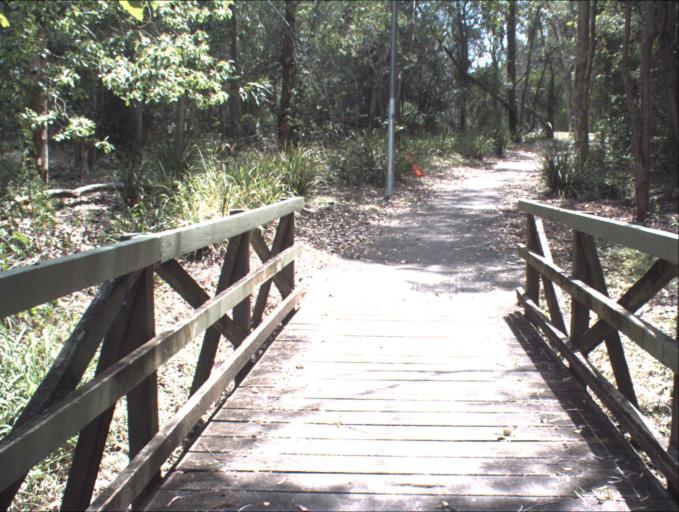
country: AU
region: Queensland
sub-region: Logan
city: Slacks Creek
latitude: -27.6432
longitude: 153.1604
